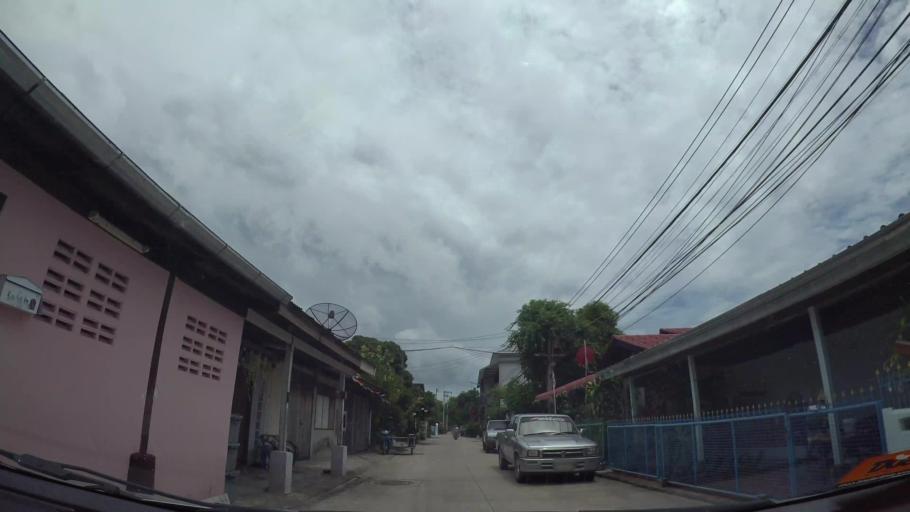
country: TH
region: Chon Buri
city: Sattahip
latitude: 12.7619
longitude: 100.8863
